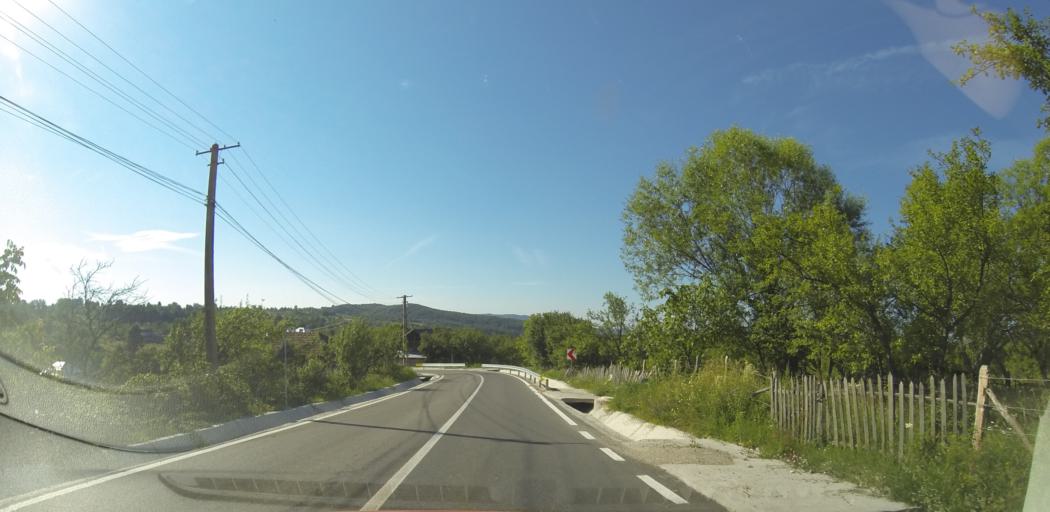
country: RO
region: Valcea
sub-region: Comuna Vaideeni
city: Vaideeni
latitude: 45.1699
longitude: 23.8771
